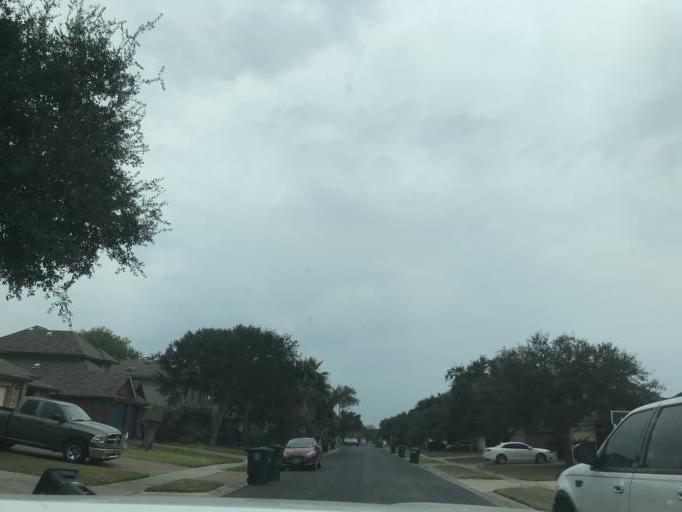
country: US
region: Texas
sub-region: Nueces County
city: Corpus Christi
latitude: 27.6703
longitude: -97.3458
